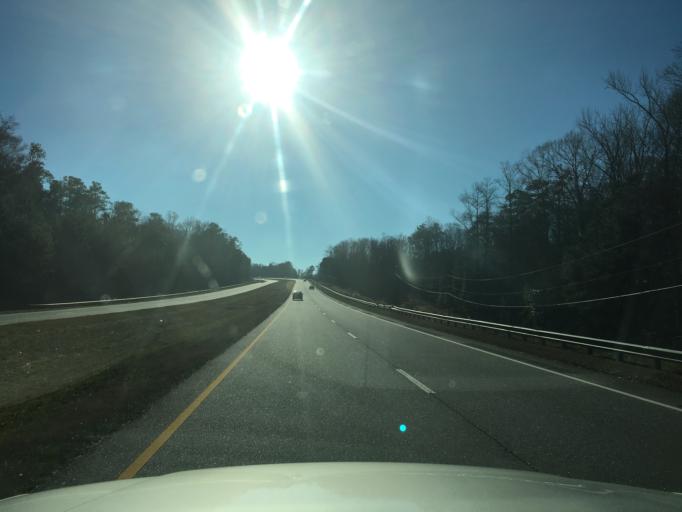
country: US
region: Georgia
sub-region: Carroll County
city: Carrollton
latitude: 33.4685
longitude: -85.1182
